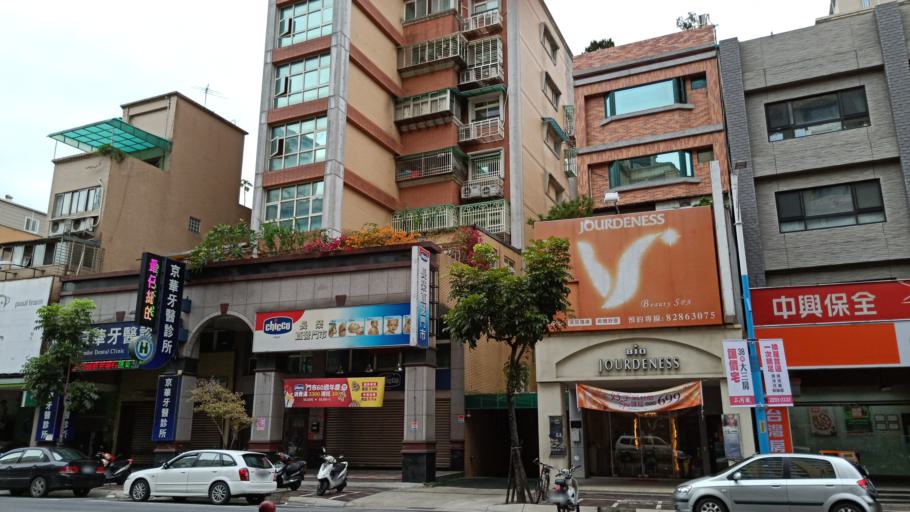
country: TW
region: Taipei
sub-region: Taipei
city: Banqiao
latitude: 25.0892
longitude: 121.4593
